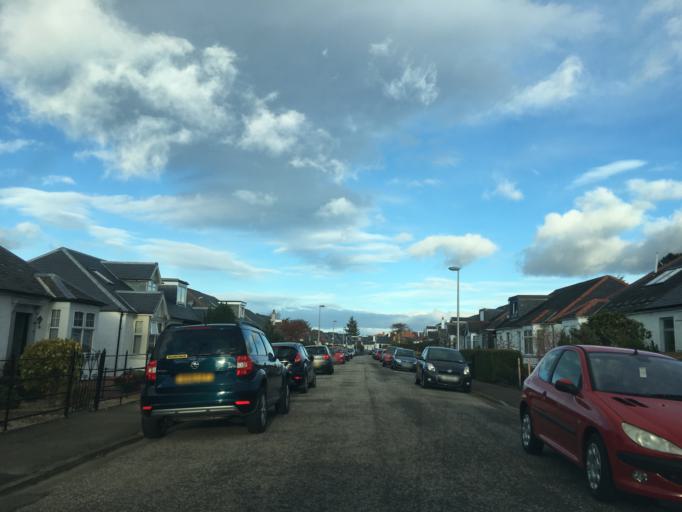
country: GB
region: Scotland
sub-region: Edinburgh
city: Colinton
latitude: 55.9184
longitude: -3.2463
